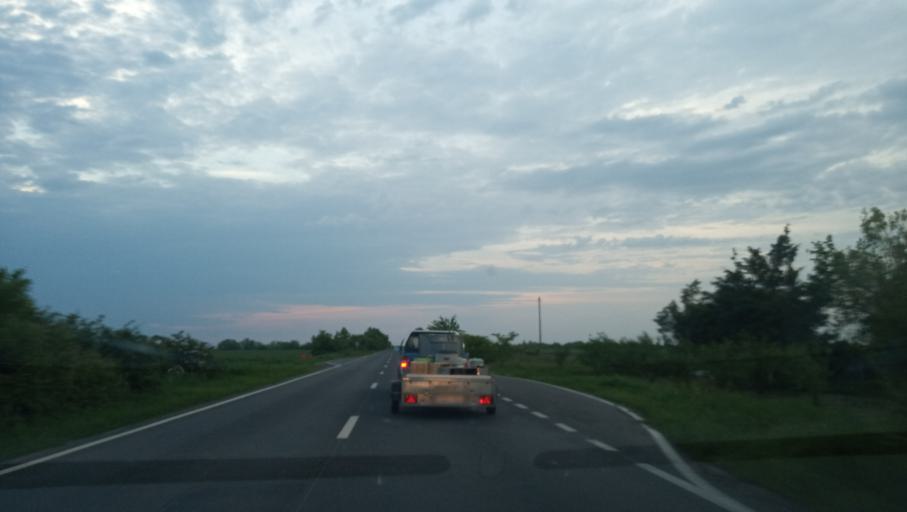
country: RO
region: Timis
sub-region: Comuna Jebel
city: Jebel
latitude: 45.5150
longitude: 21.2353
